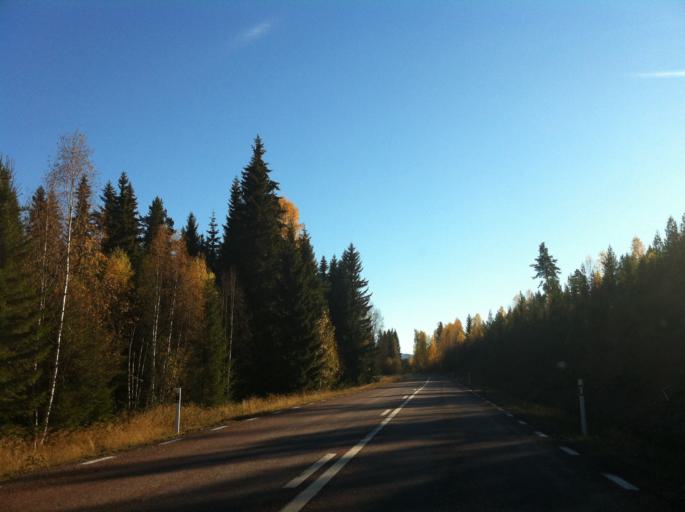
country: SE
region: Dalarna
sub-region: Alvdalens Kommun
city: AElvdalen
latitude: 61.1727
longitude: 14.1037
